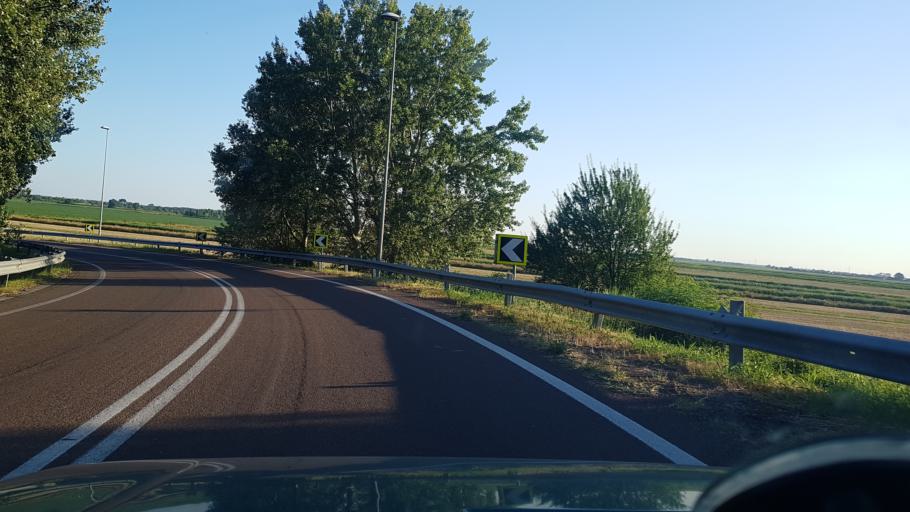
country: IT
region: Veneto
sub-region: Provincia di Venezia
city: Bibione
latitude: 45.6721
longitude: 13.0534
